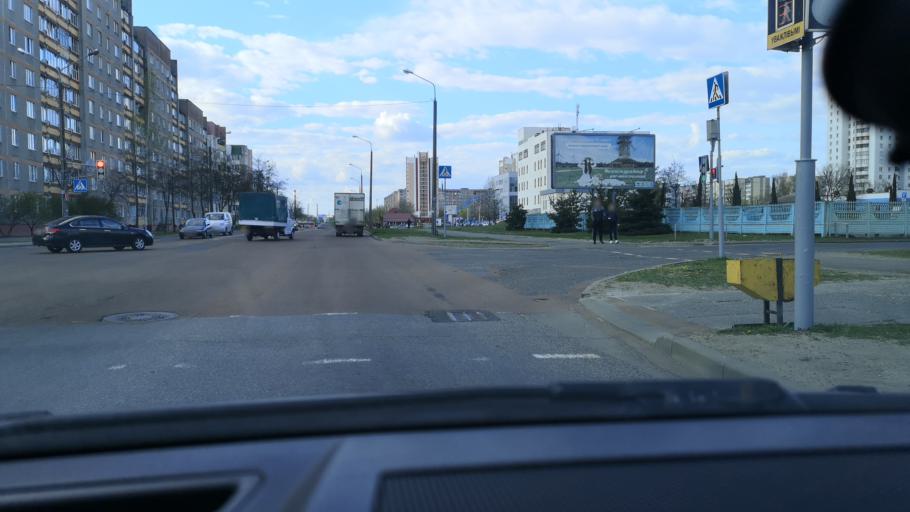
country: BY
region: Gomel
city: Gomel
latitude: 52.4026
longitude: 30.9211
